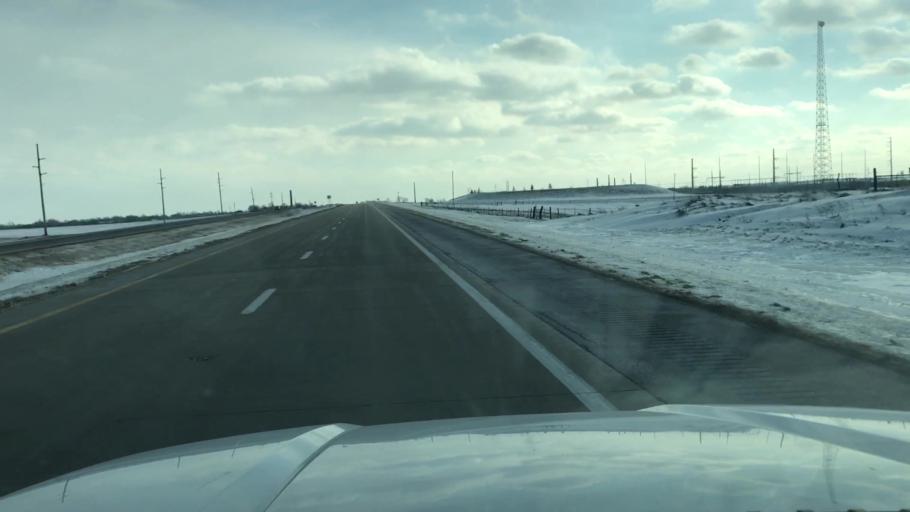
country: US
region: Missouri
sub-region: Nodaway County
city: Maryville
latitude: 40.2325
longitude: -94.8680
